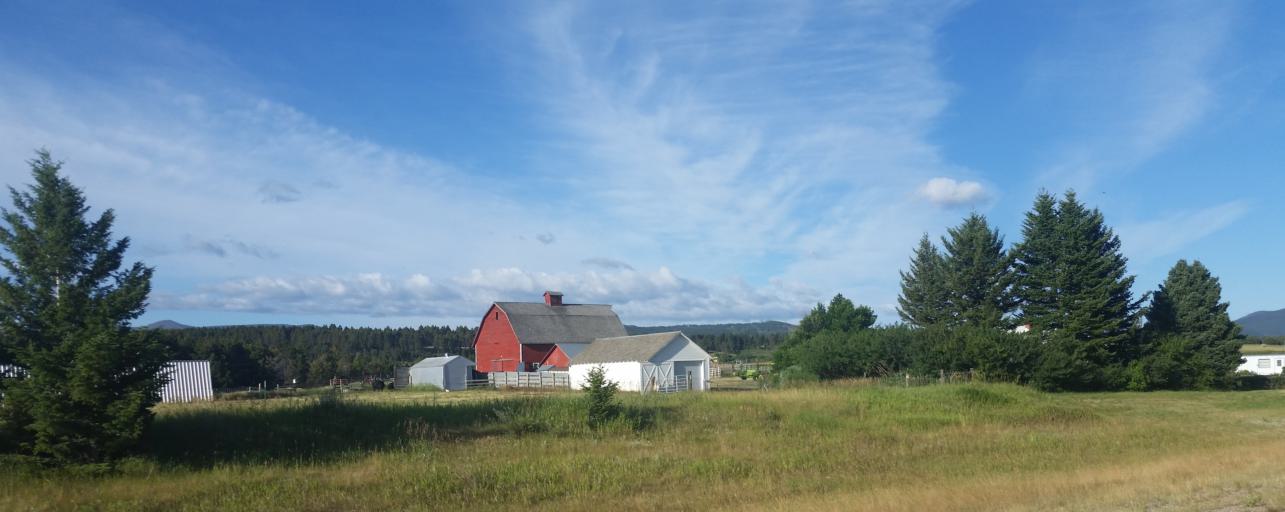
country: US
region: Montana
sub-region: Cascade County
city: Malmstrom Air Force Base
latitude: 47.1697
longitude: -110.8616
